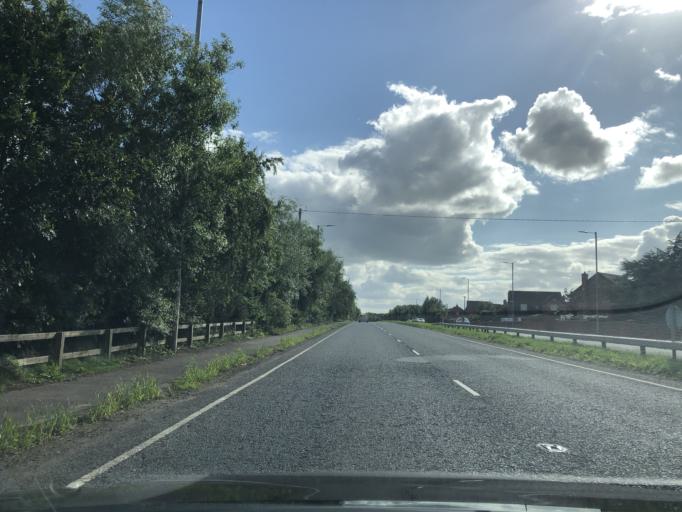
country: GB
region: Northern Ireland
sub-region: Ards District
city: Comber
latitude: 54.5546
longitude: -5.7230
